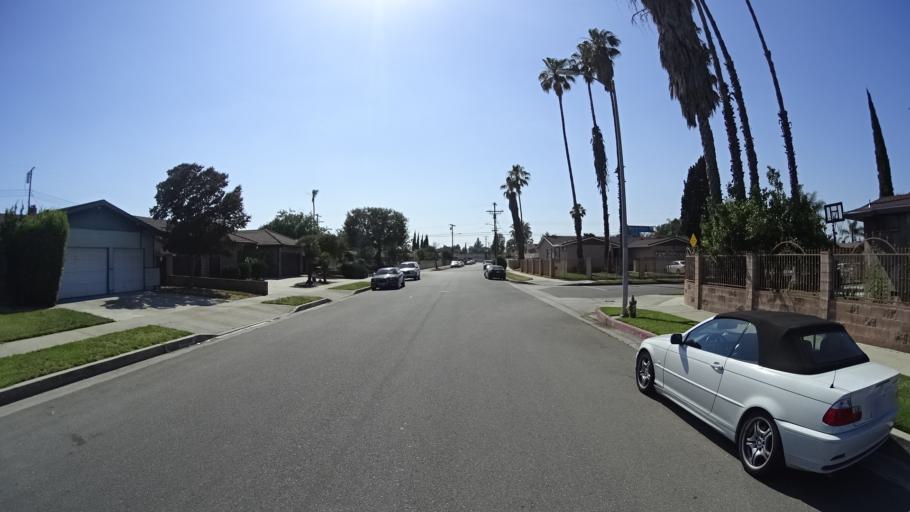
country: US
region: California
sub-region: Los Angeles County
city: Van Nuys
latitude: 34.2092
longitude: -118.4195
